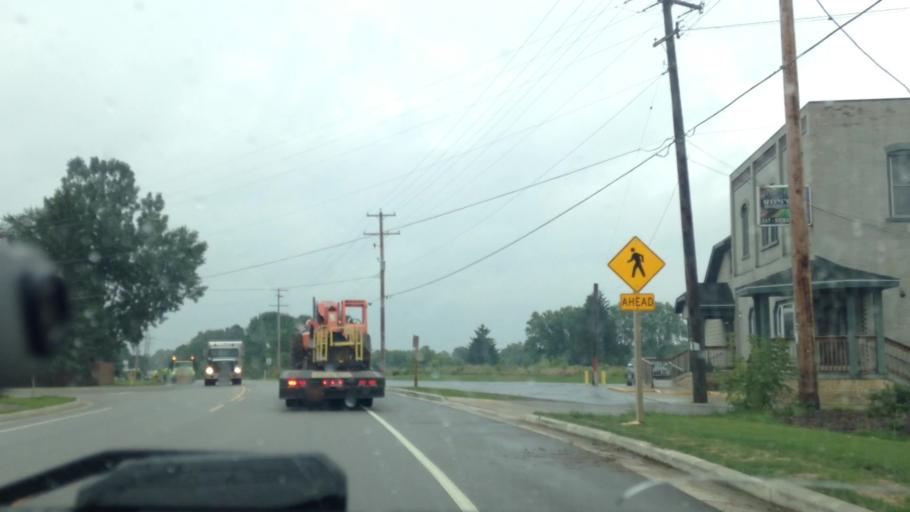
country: US
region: Wisconsin
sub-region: Washington County
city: Slinger
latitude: 43.3102
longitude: -88.2586
